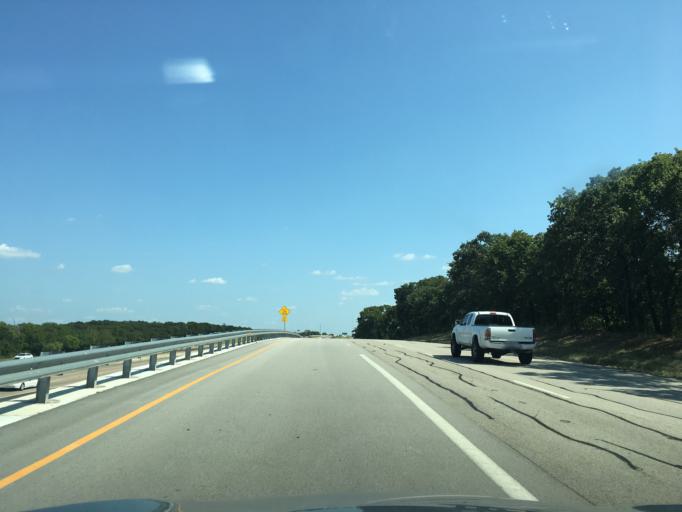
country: US
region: Texas
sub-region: Tarrant County
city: Kennedale
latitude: 32.6526
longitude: -97.1906
